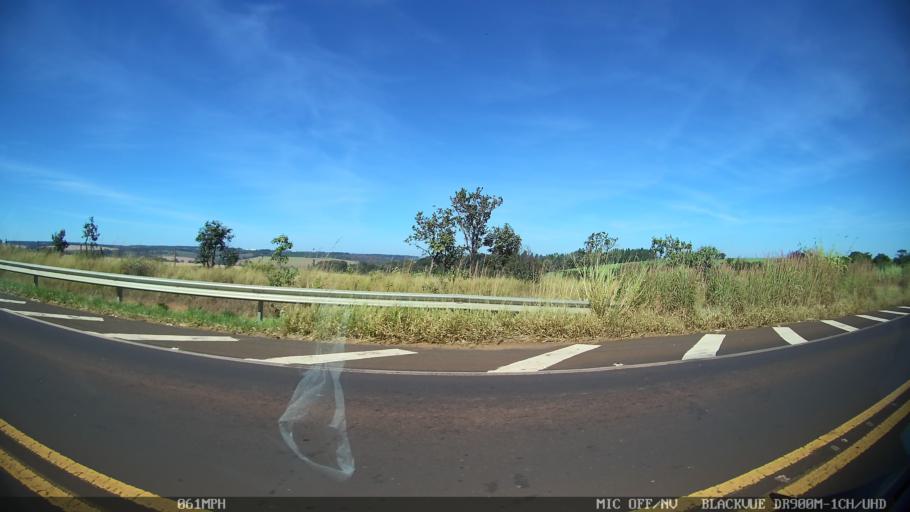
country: BR
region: Sao Paulo
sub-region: Franca
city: Franca
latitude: -20.5556
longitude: -47.4962
